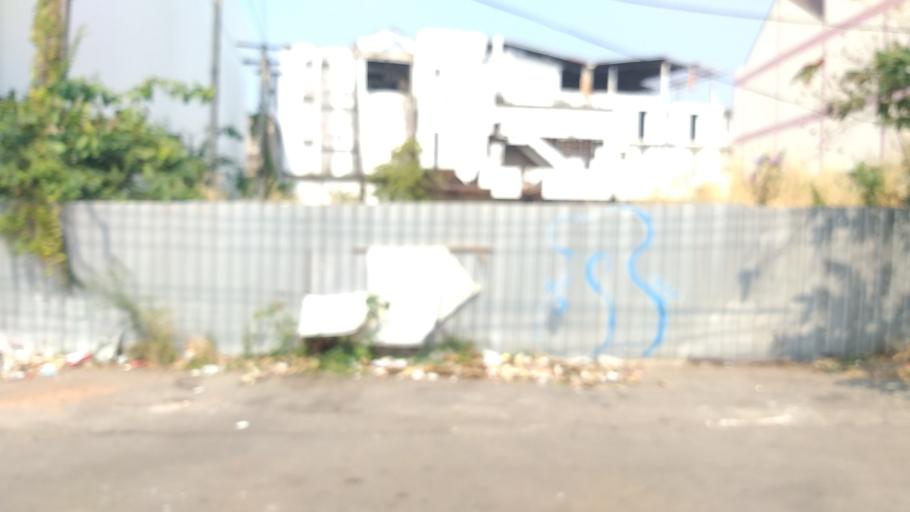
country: TH
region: Changwat Udon Thani
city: Udon Thani
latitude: 17.4037
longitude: 102.7953
